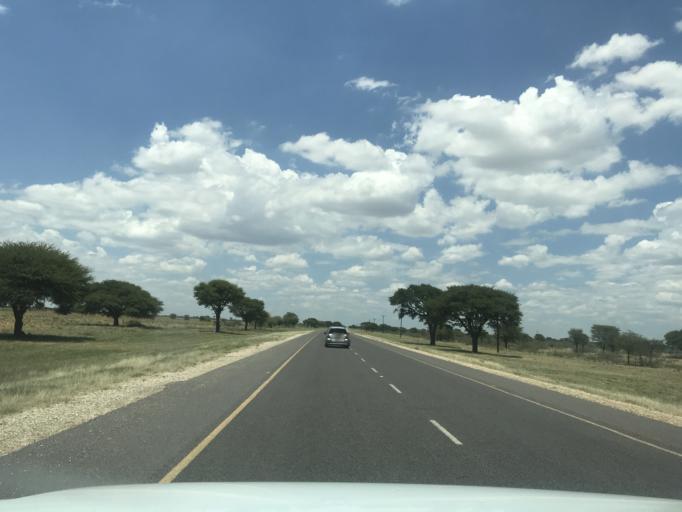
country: BW
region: South East
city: Janeng
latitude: -25.6451
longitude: 25.1494
